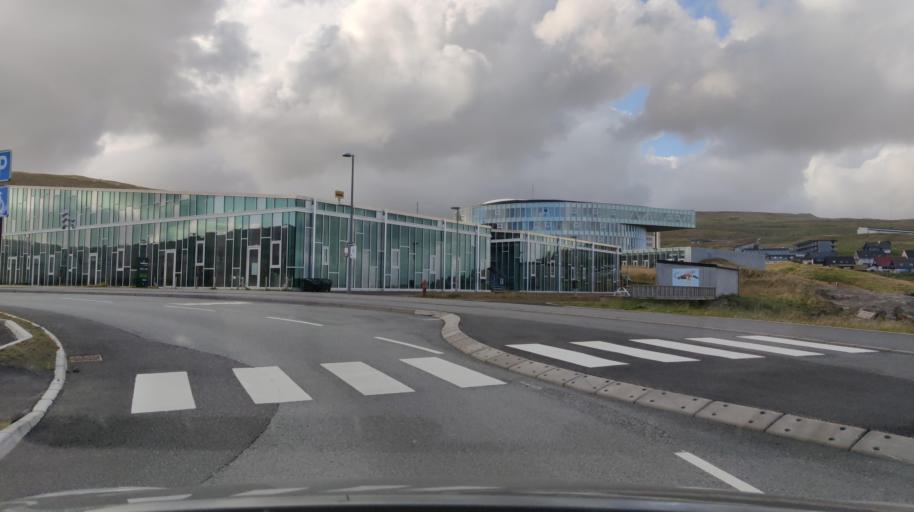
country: FO
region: Streymoy
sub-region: Torshavn
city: Torshavn
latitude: 62.0049
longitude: -6.7958
